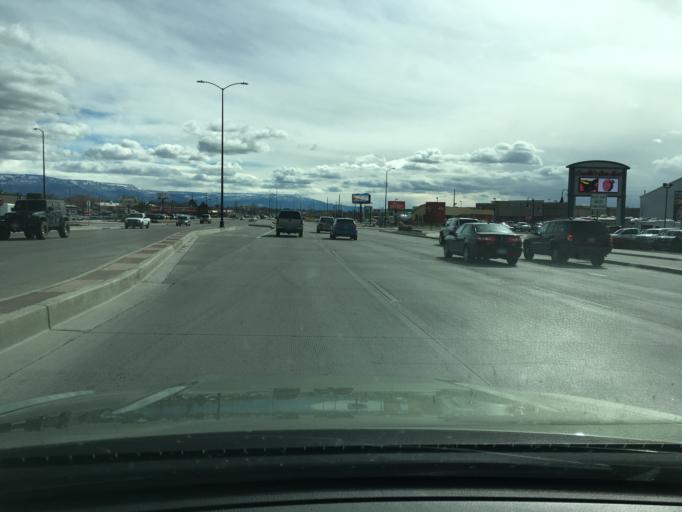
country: US
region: Colorado
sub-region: Mesa County
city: Grand Junction
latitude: 39.0825
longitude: -108.5885
